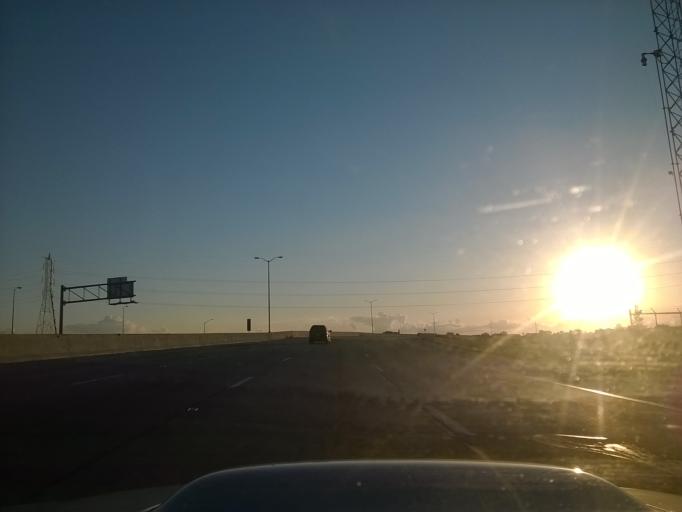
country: US
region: Indiana
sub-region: Marion County
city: Speedway
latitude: 39.8240
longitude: -86.2241
